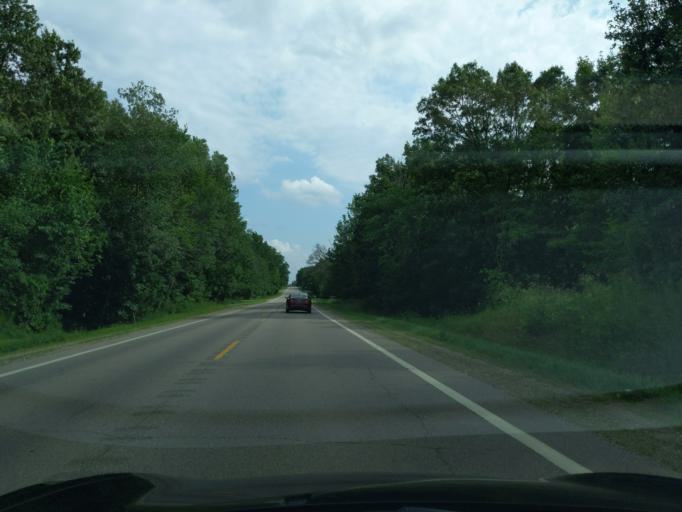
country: US
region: Michigan
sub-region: Eaton County
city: Eaton Rapids
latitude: 42.4320
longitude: -84.6497
